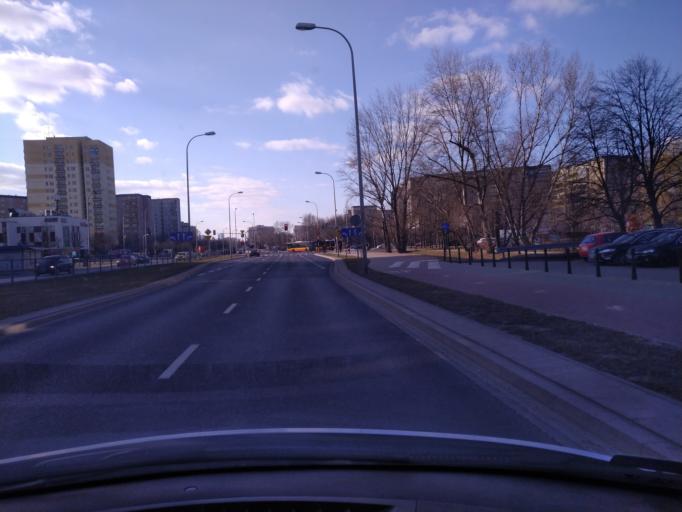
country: PL
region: Masovian Voivodeship
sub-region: Warszawa
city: Praga Poludnie
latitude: 52.2247
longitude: 21.0944
